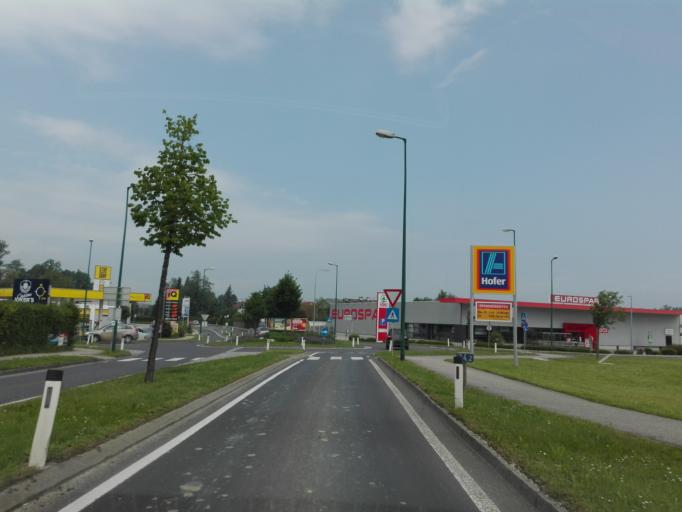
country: AT
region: Upper Austria
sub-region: Politischer Bezirk Urfahr-Umgebung
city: Feldkirchen an der Donau
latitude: 48.3014
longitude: 14.0308
